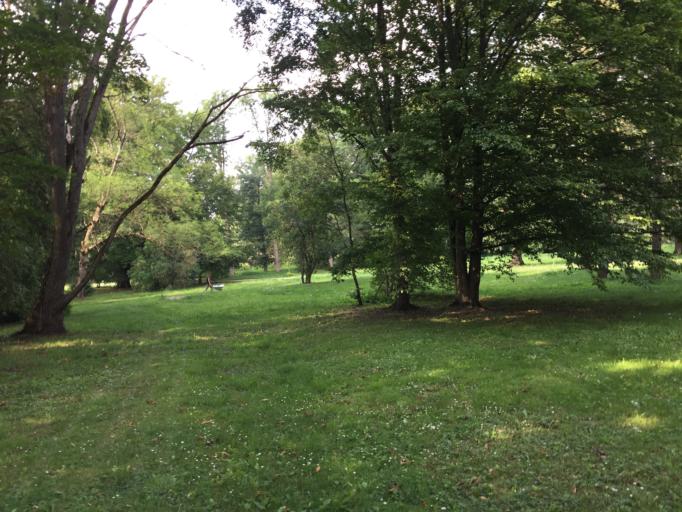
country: LV
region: Auces Novads
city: Auce
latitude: 56.4690
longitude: 22.8871
